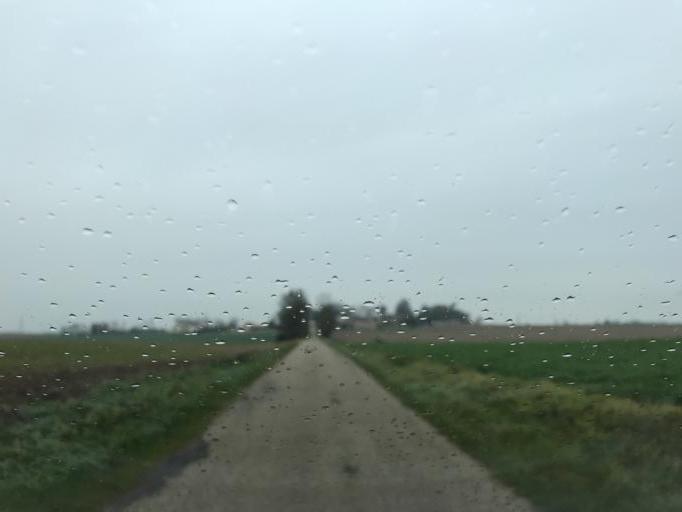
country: FR
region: Rhone-Alpes
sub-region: Departement de l'Ain
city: Saint-Maurice-de-Beynost
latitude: 45.8462
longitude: 4.9788
